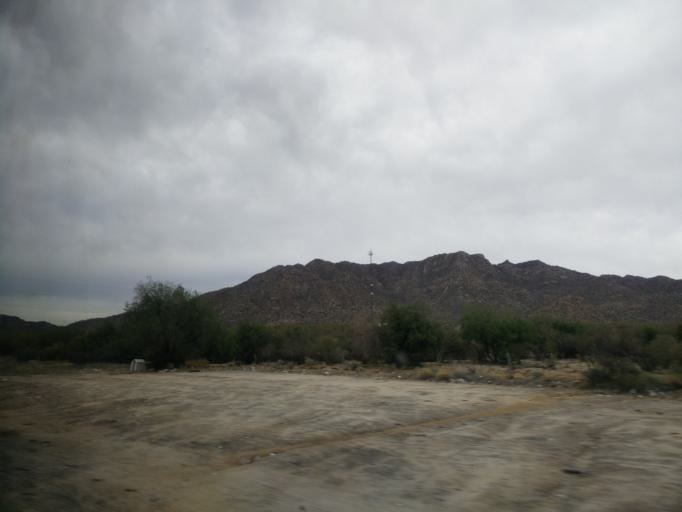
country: MX
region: Sonora
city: Hermosillo
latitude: 28.9671
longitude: -110.9635
